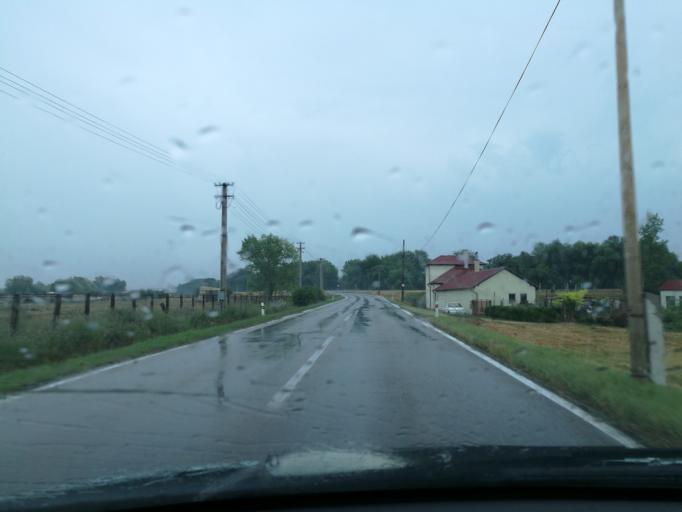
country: HU
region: Komarom-Esztergom
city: Almasfuzito
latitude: 47.7455
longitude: 18.2398
